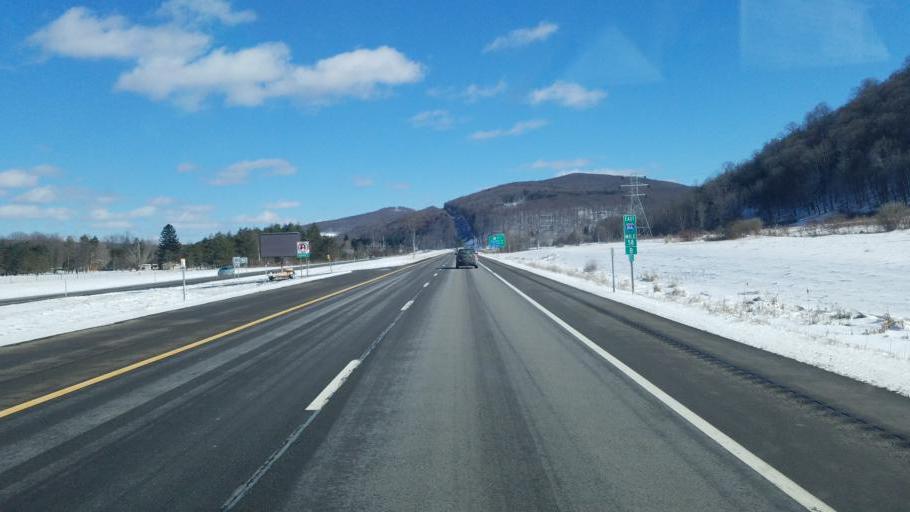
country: US
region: New York
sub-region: Cattaraugus County
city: Salamanca
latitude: 42.1524
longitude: -78.7407
